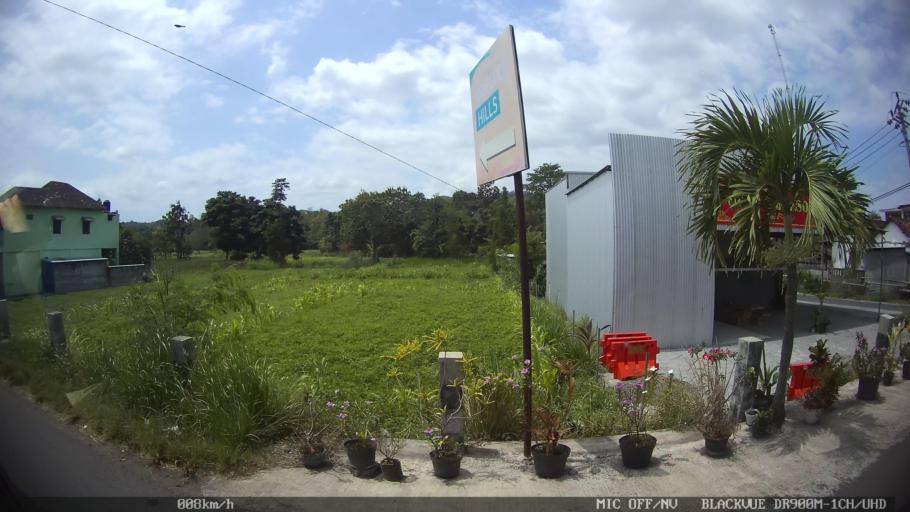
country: ID
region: Central Java
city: Candi Prambanan
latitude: -7.7834
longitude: 110.4892
